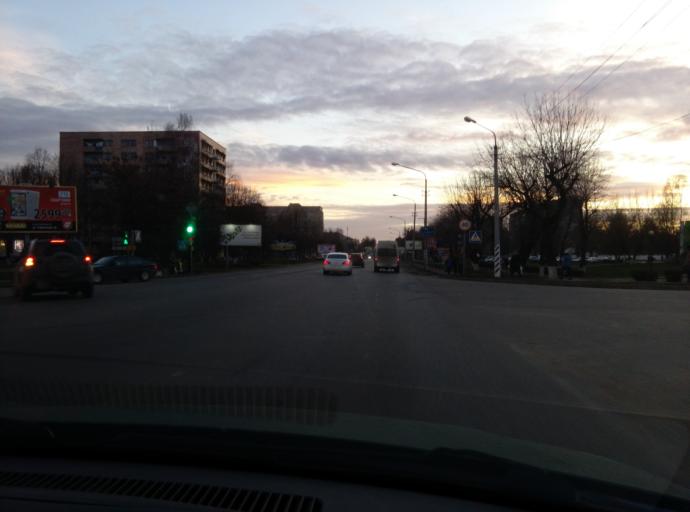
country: BY
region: Minsk
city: Horad Barysaw
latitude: 54.2197
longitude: 28.4914
